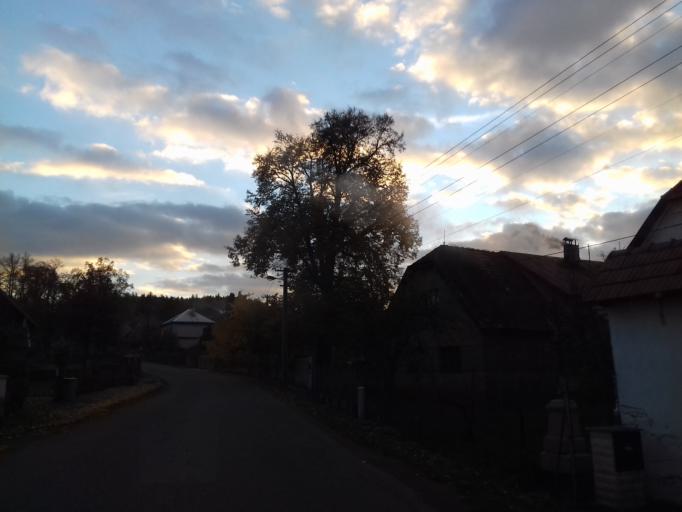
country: CZ
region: Pardubicky
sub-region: Okres Chrudim
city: Skutec
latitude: 49.8153
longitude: 15.9572
